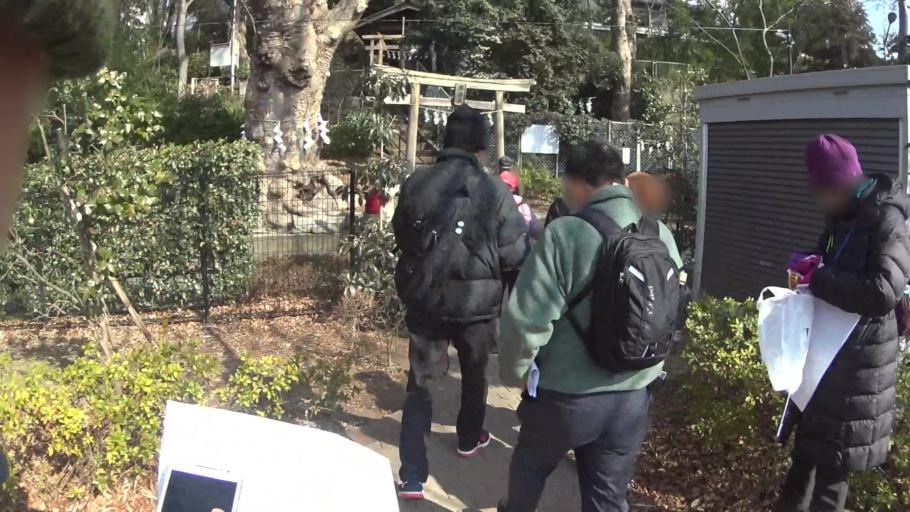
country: JP
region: Tokyo
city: Kokubunji
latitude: 35.6658
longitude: 139.4949
